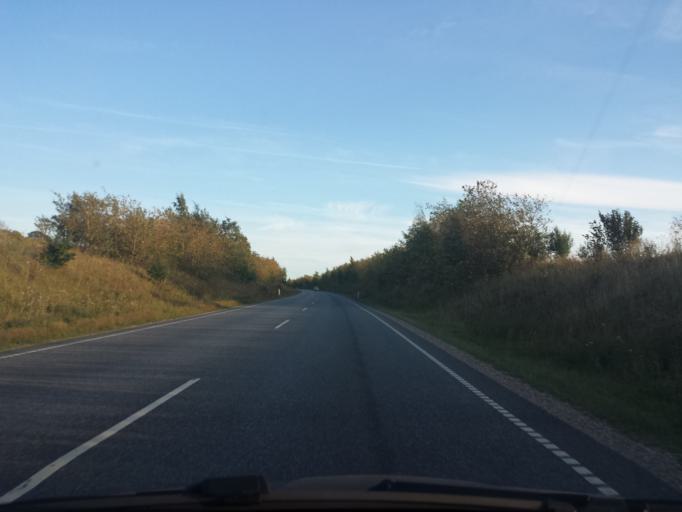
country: DK
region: Zealand
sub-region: Roskilde Kommune
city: Jyllinge
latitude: 55.8005
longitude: 12.1033
